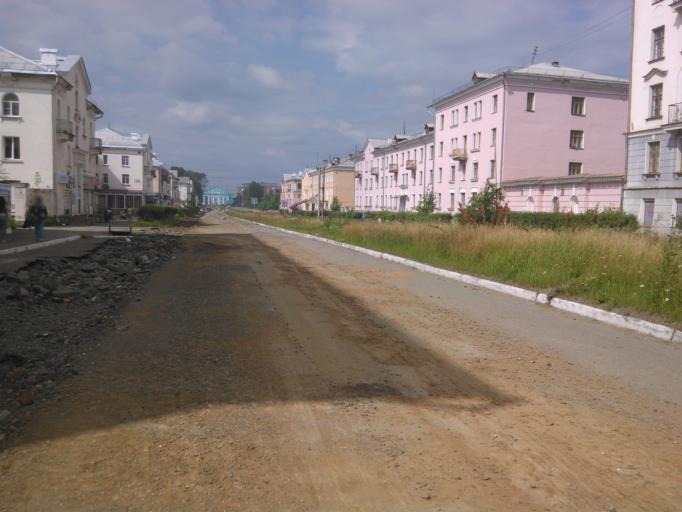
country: RU
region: Sverdlovsk
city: Krasnotur'insk
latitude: 59.7637
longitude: 60.1919
